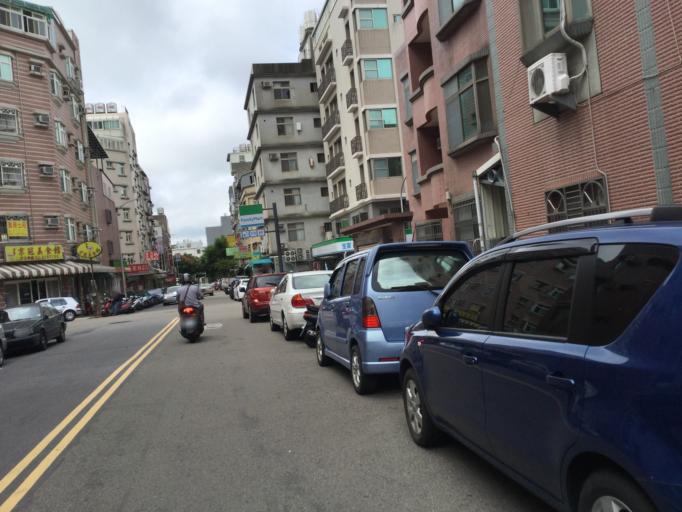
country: TW
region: Taiwan
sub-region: Hsinchu
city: Hsinchu
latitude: 24.7771
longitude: 121.0213
